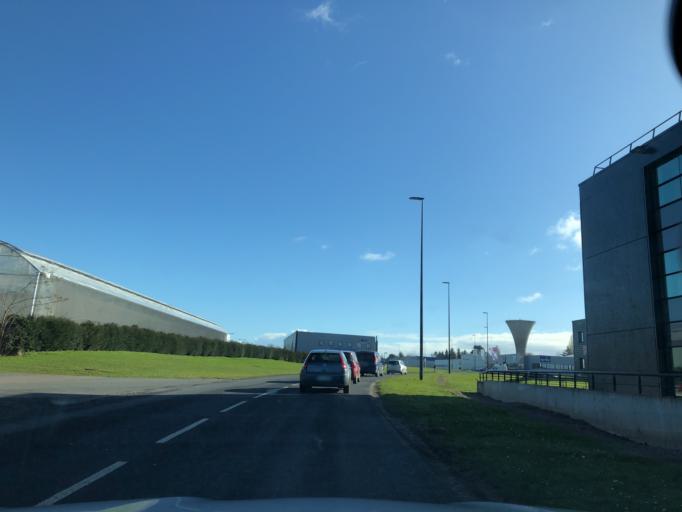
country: FR
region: Lower Normandy
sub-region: Departement du Calvados
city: Epron
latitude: 49.2163
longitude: -0.3491
